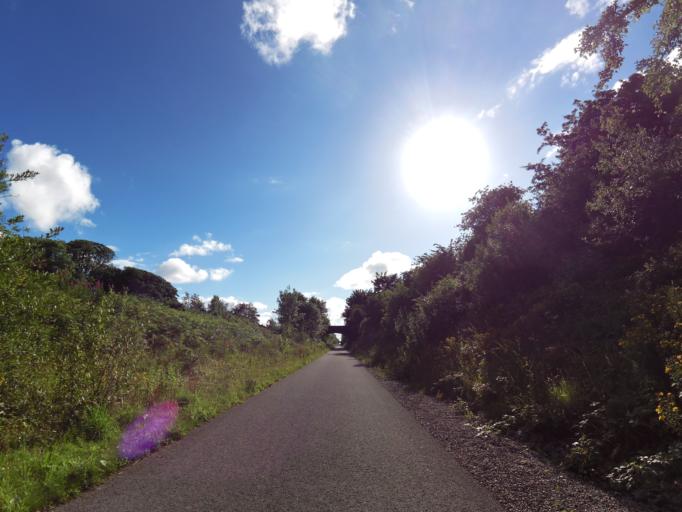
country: IE
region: Leinster
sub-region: An Iarmhi
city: Moate
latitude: 53.4106
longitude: -7.6623
